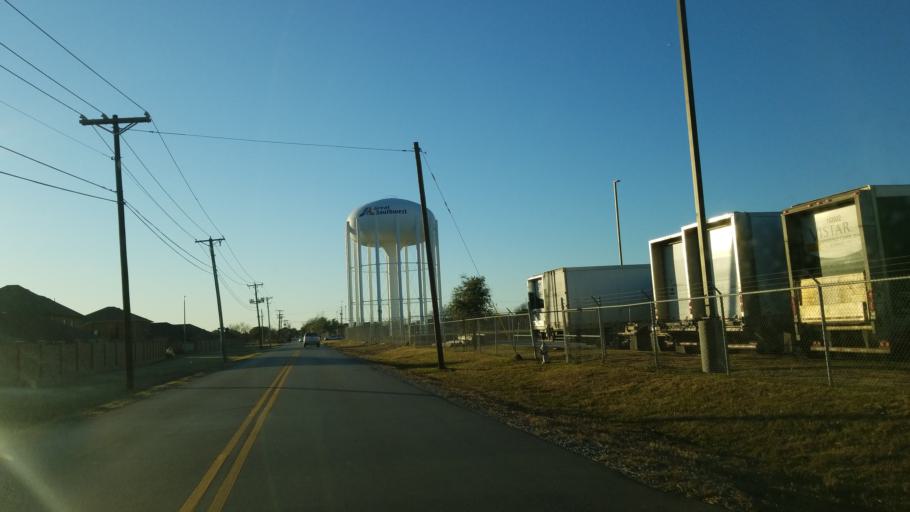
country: US
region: Texas
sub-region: Dallas County
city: Grand Prairie
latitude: 32.7352
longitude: -97.0515
